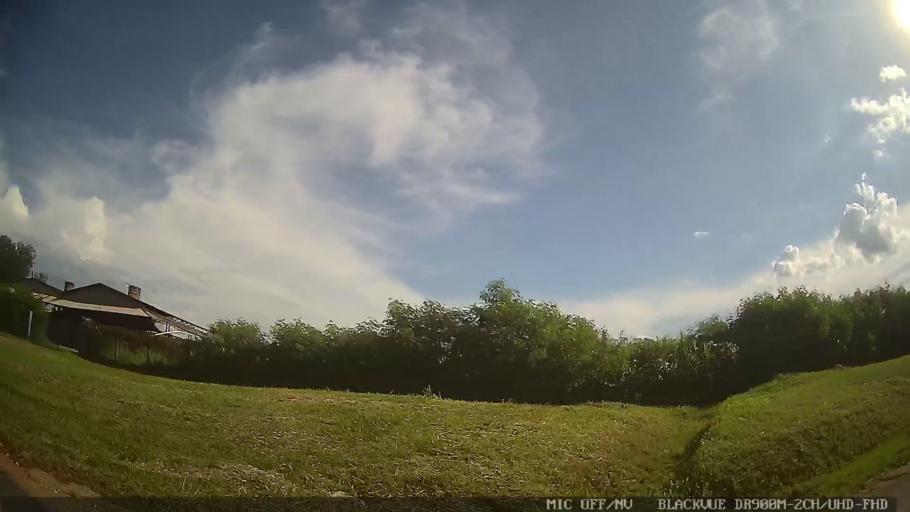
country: BR
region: Sao Paulo
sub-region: Laranjal Paulista
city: Laranjal Paulista
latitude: -23.0780
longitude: -47.8035
